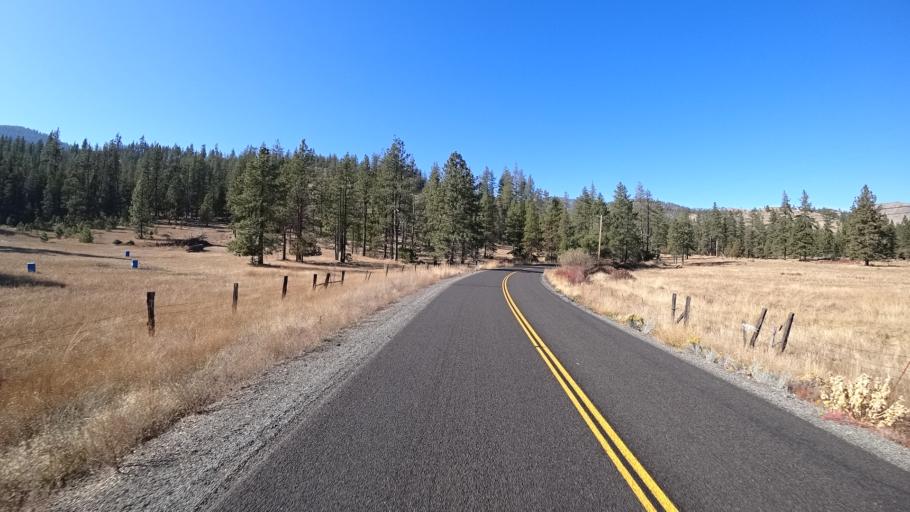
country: US
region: California
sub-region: Siskiyou County
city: Weed
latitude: 41.4356
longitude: -122.4612
